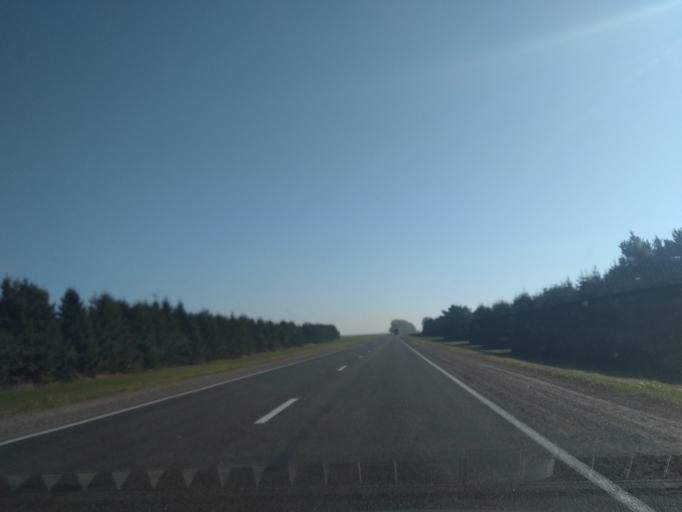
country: BY
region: Grodnenskaya
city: Slonim
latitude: 53.1232
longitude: 25.0788
